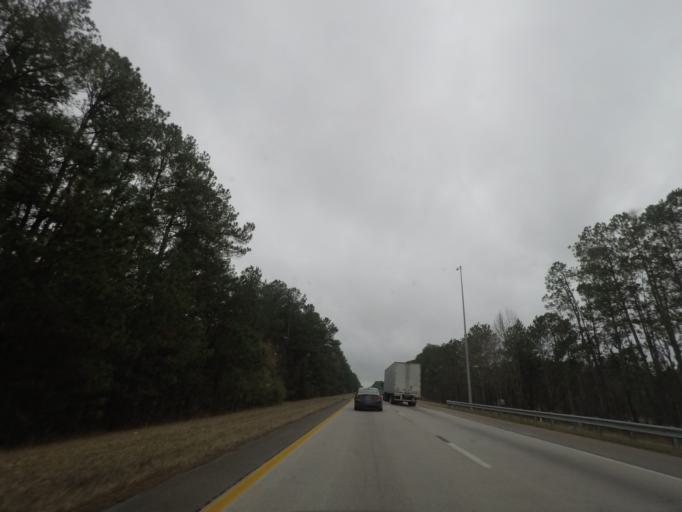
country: US
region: South Carolina
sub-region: Colleton County
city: Walterboro
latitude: 33.0120
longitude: -80.6676
